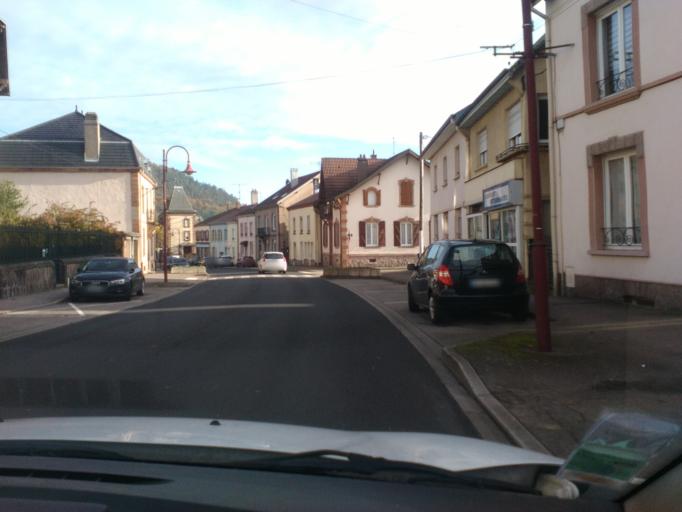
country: FR
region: Lorraine
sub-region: Departement des Vosges
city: Etival-Clairefontaine
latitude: 48.4041
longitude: 6.8394
